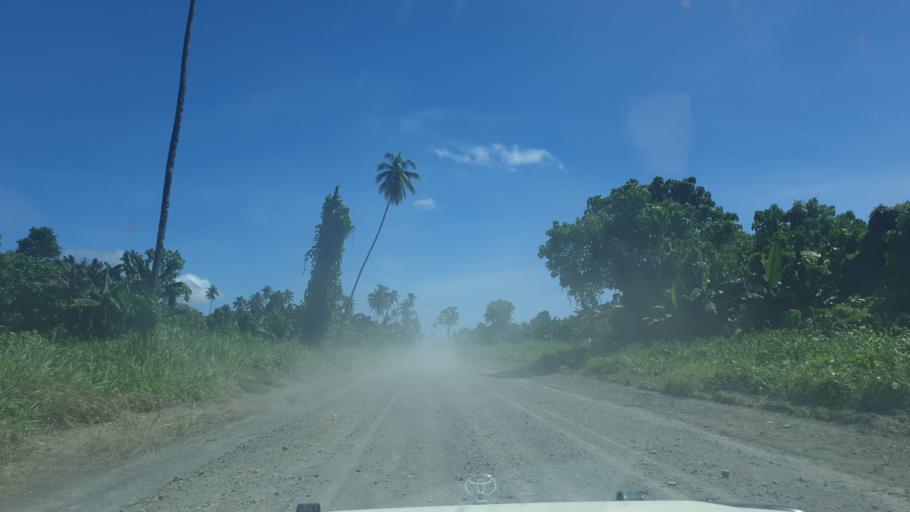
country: PG
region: Bougainville
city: Arawa
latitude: -5.9806
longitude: 155.3530
